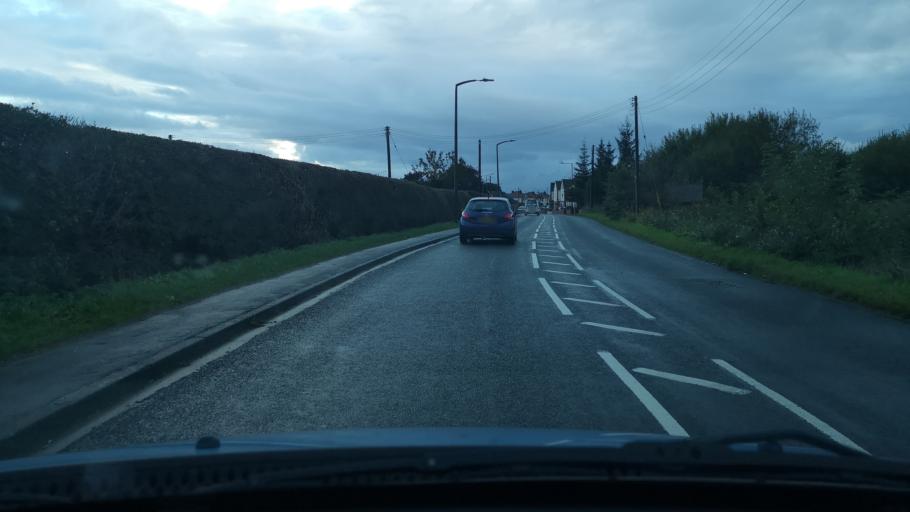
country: GB
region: England
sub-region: Doncaster
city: Askern
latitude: 53.6179
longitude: -1.1374
